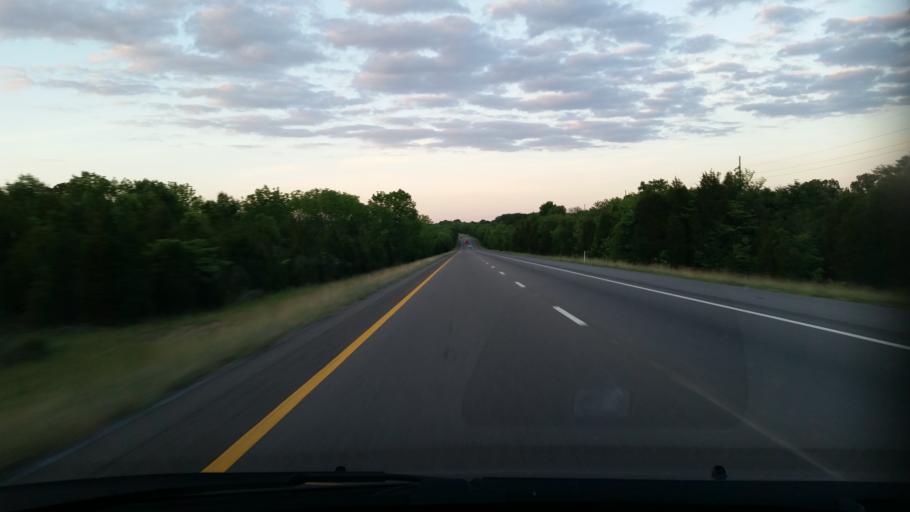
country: US
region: Tennessee
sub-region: Greene County
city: Mosheim
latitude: 36.2437
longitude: -82.9841
